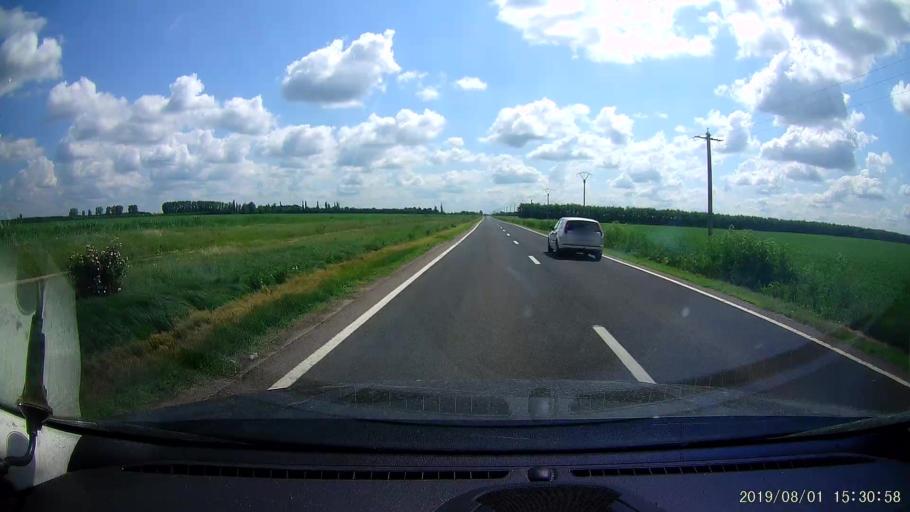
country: RO
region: Braila
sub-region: Comuna Viziru
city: Viziru
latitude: 44.9534
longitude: 27.6670
